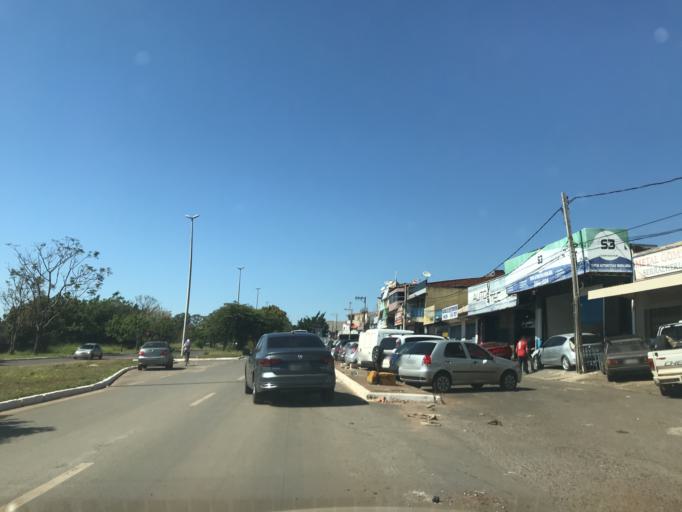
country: BR
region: Federal District
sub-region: Brasilia
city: Brasilia
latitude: -15.8012
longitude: -48.0930
